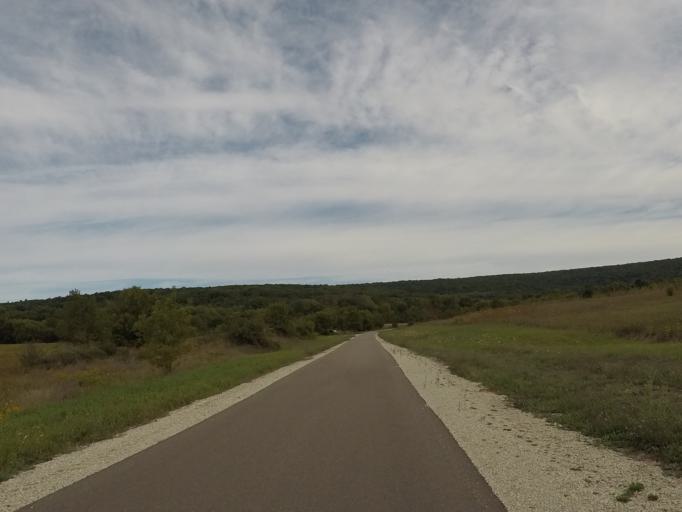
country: US
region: Wisconsin
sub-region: Sauk County
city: Prairie du Sac
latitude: 43.3777
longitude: -89.7352
